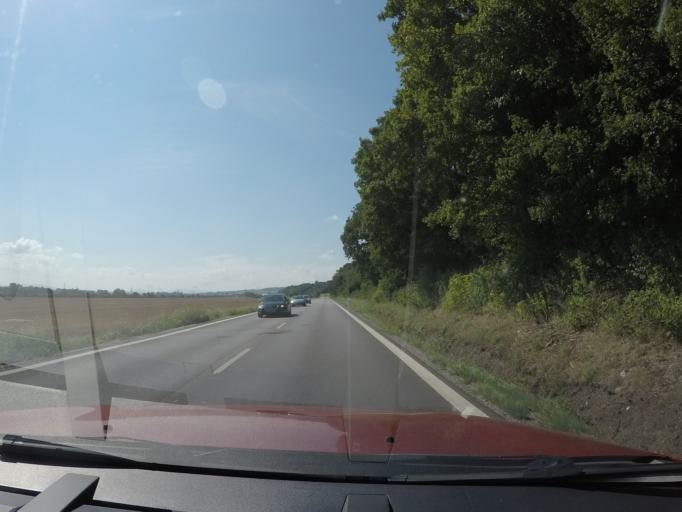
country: SK
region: Presovsky
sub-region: Okres Presov
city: Presov
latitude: 48.8945
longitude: 21.2438
